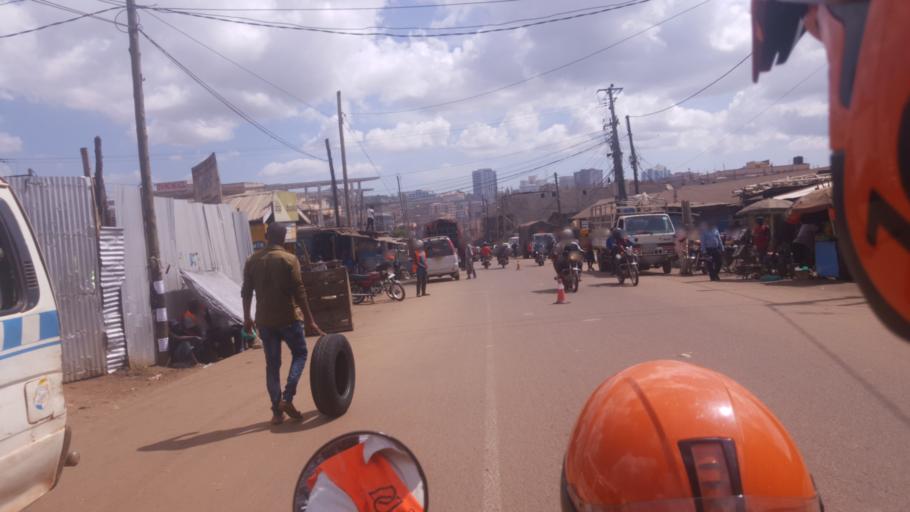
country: UG
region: Central Region
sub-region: Kampala District
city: Kampala
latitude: 0.3087
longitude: 32.5701
